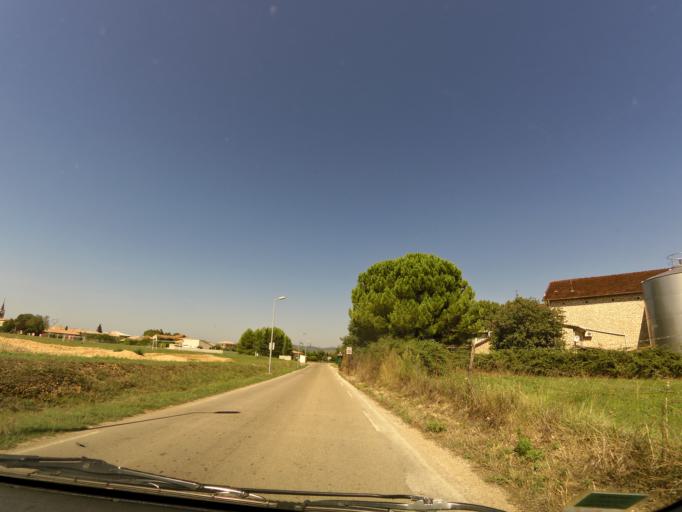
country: FR
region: Languedoc-Roussillon
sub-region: Departement du Gard
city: Villevieille
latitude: 43.8298
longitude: 4.0925
